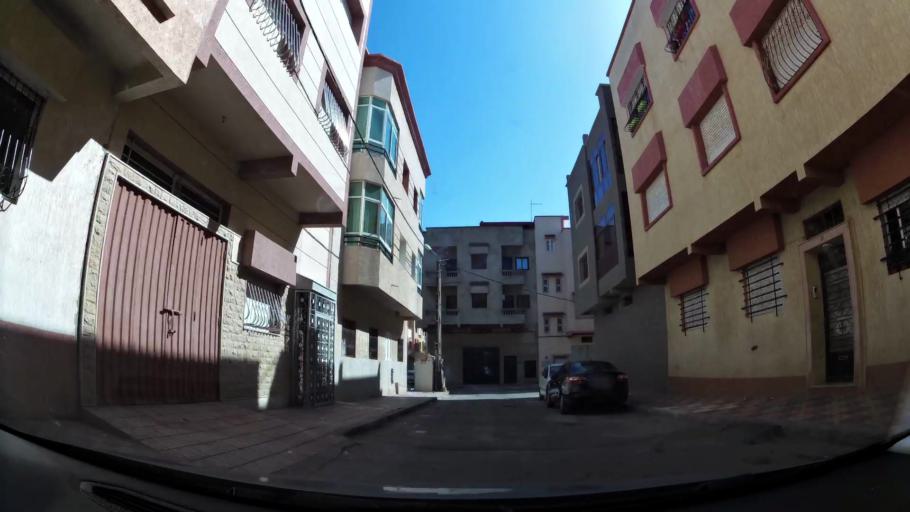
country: MA
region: Rabat-Sale-Zemmour-Zaer
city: Sale
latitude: 34.0658
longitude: -6.8012
